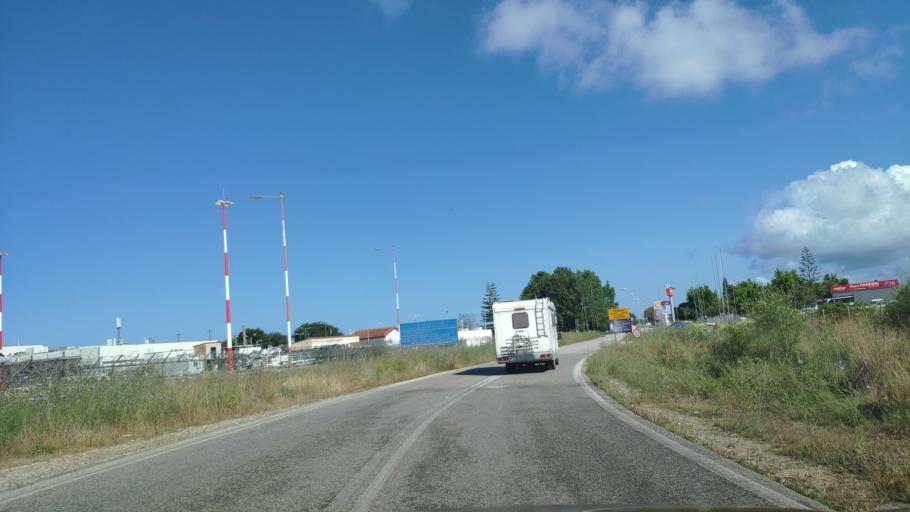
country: GR
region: Epirus
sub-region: Nomos Prevezis
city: Preveza
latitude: 38.9305
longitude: 20.7745
